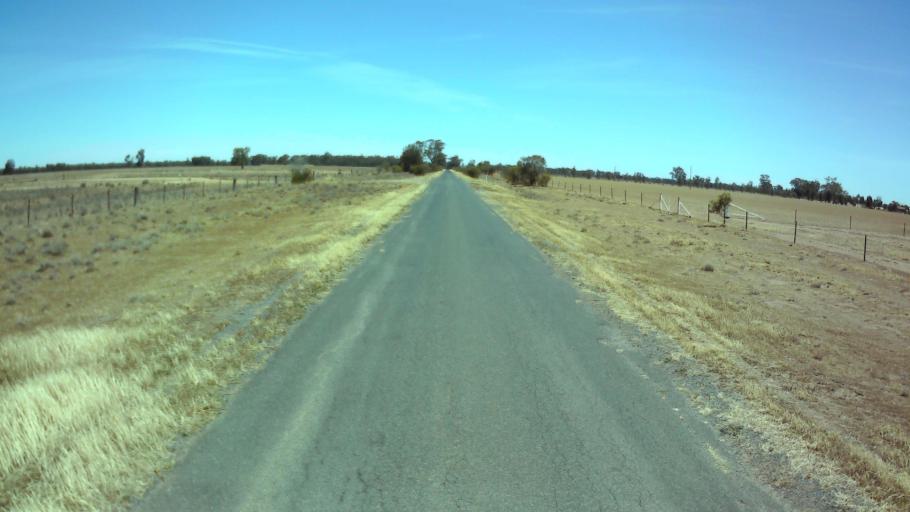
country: AU
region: New South Wales
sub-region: Weddin
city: Grenfell
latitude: -33.8912
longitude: 147.6882
